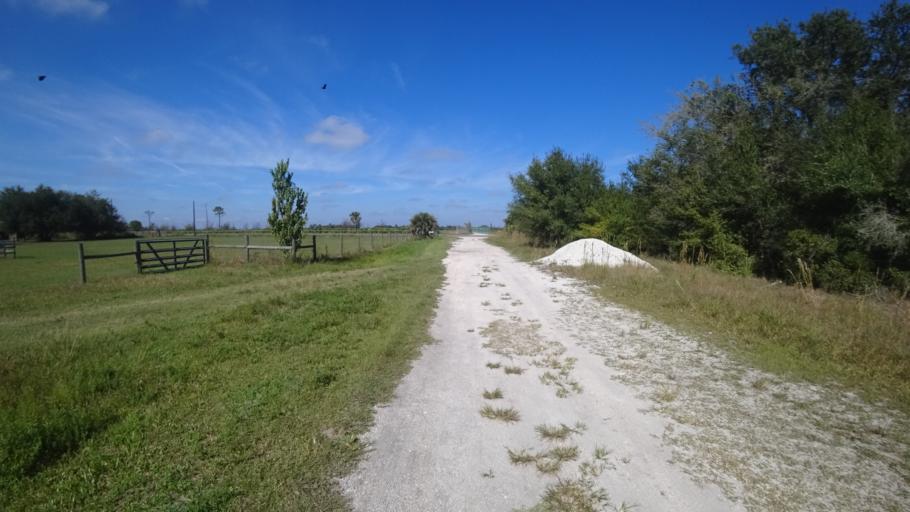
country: US
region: Florida
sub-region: DeSoto County
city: Arcadia
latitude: 27.2943
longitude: -82.0644
